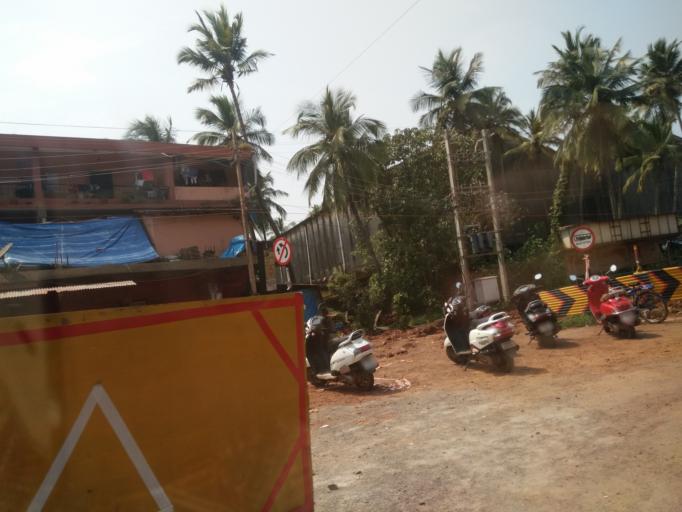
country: IN
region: Goa
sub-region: South Goa
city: Cortalim
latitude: 15.3980
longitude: 73.9106
